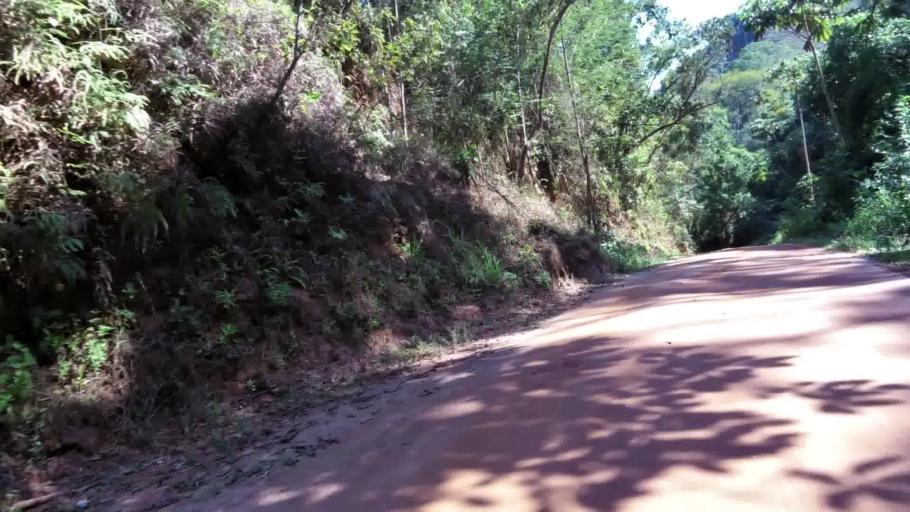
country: BR
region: Espirito Santo
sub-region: Alfredo Chaves
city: Alfredo Chaves
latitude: -20.5725
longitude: -40.7874
